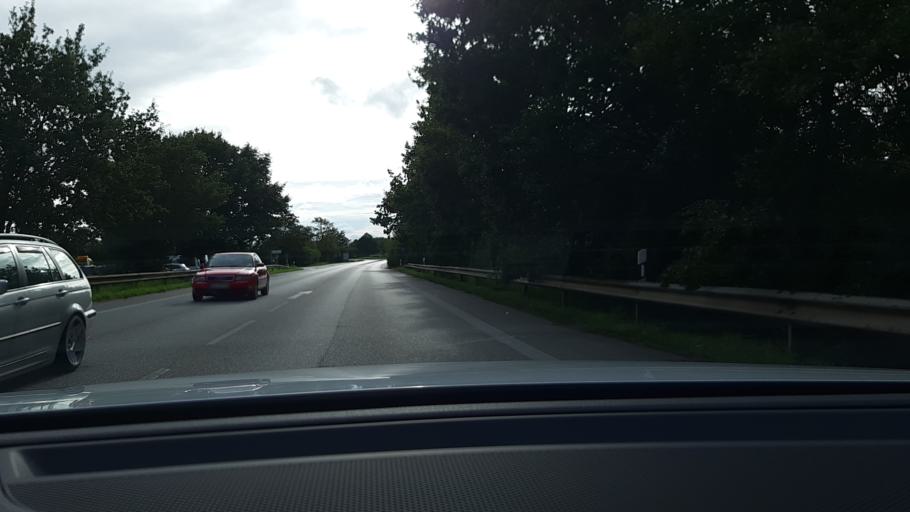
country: DE
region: Schleswig-Holstein
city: Stockelsdorf
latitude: 53.8919
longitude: 10.6225
